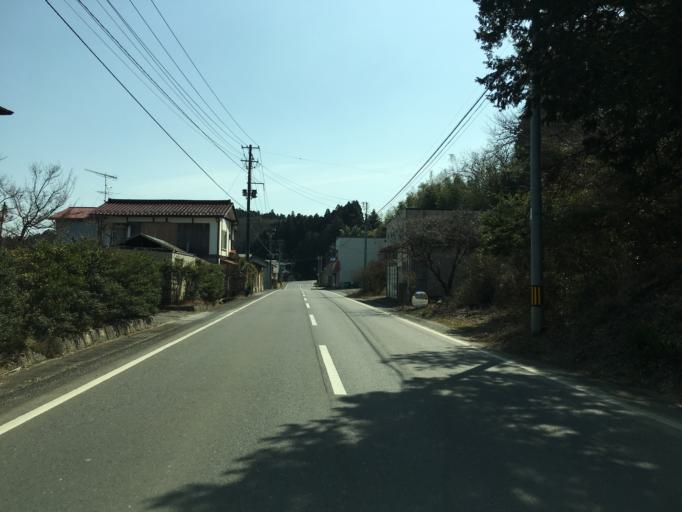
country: JP
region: Fukushima
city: Ishikawa
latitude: 37.1439
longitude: 140.4001
